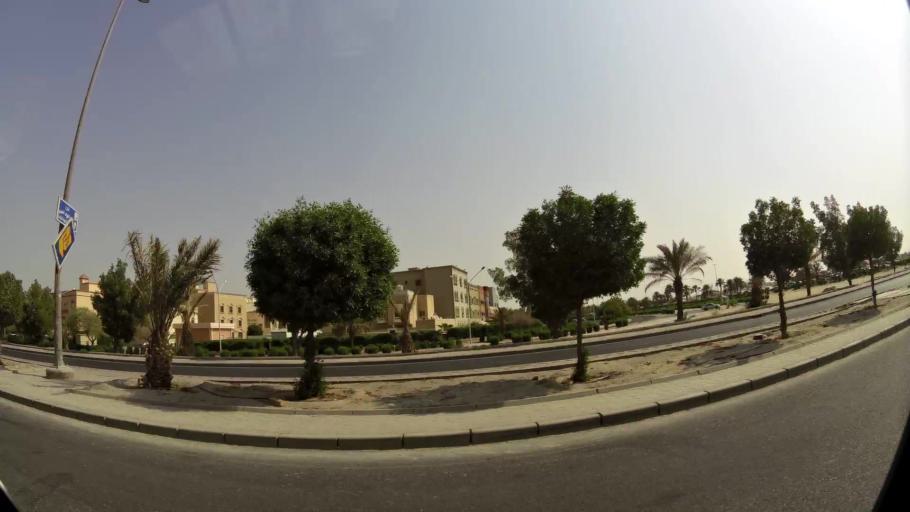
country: KW
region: Muhafazat al Jahra'
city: Al Jahra'
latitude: 29.3360
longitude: 47.6840
